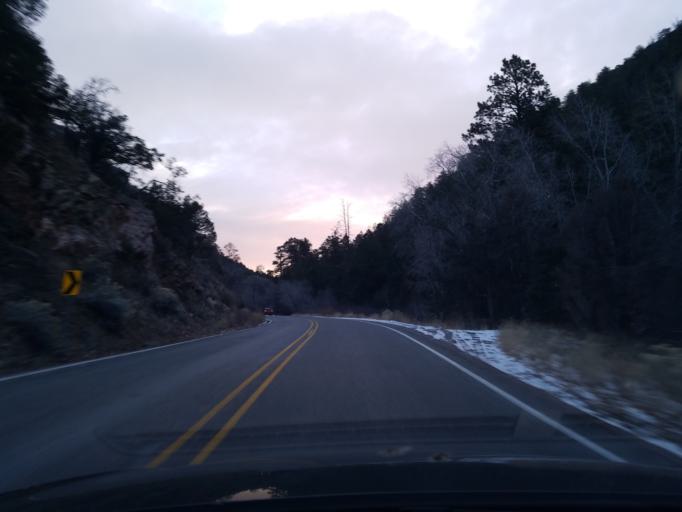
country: US
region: New Mexico
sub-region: Santa Fe County
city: Santa Fe
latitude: 35.7280
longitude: -105.8783
